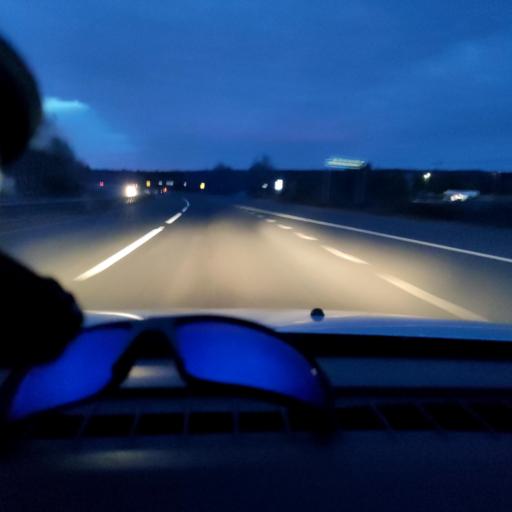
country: RU
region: Samara
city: Novokuybyshevsk
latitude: 53.0548
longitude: 50.0164
